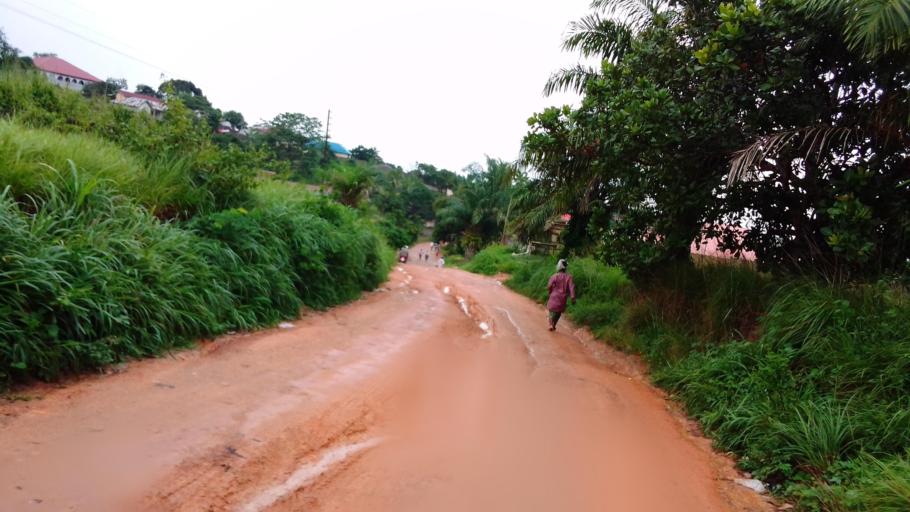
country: SL
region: Eastern Province
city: Kenema
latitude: 7.8981
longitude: -11.1833
